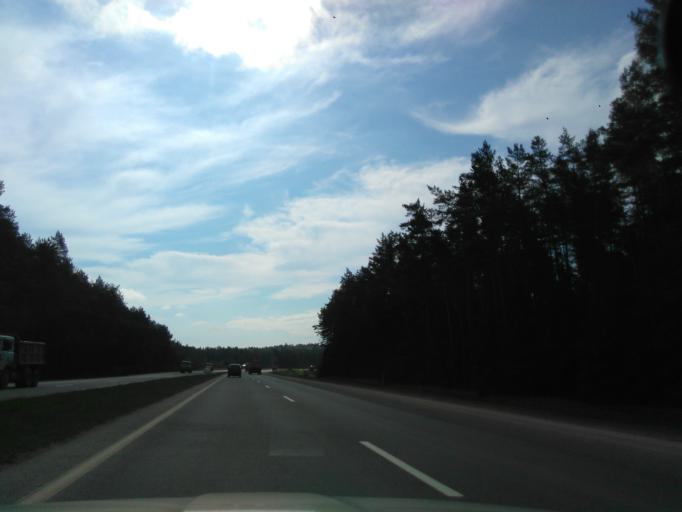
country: BY
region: Minsk
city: Rakaw
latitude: 53.9591
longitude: 27.1055
